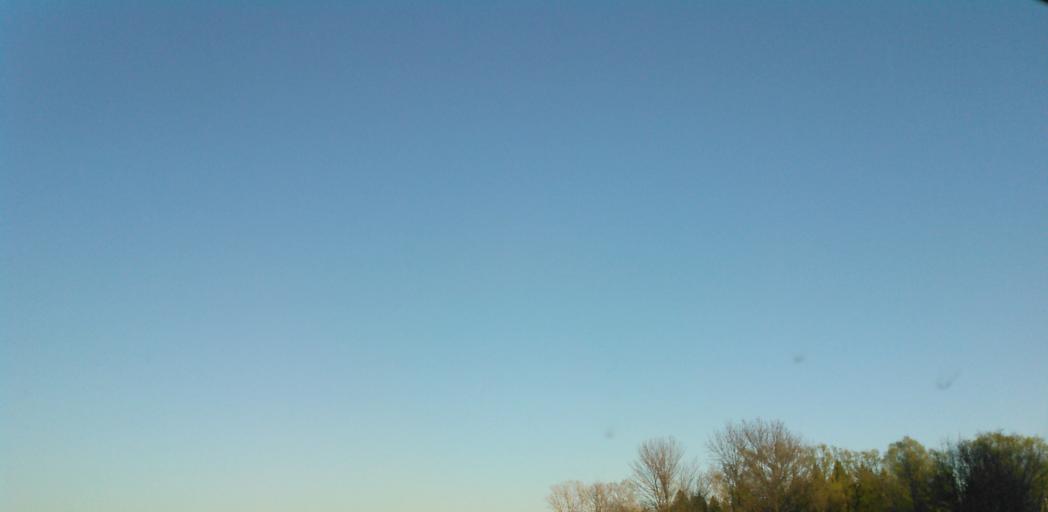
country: US
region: New York
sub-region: Monroe County
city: Pittsford
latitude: 43.0469
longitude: -77.5740
